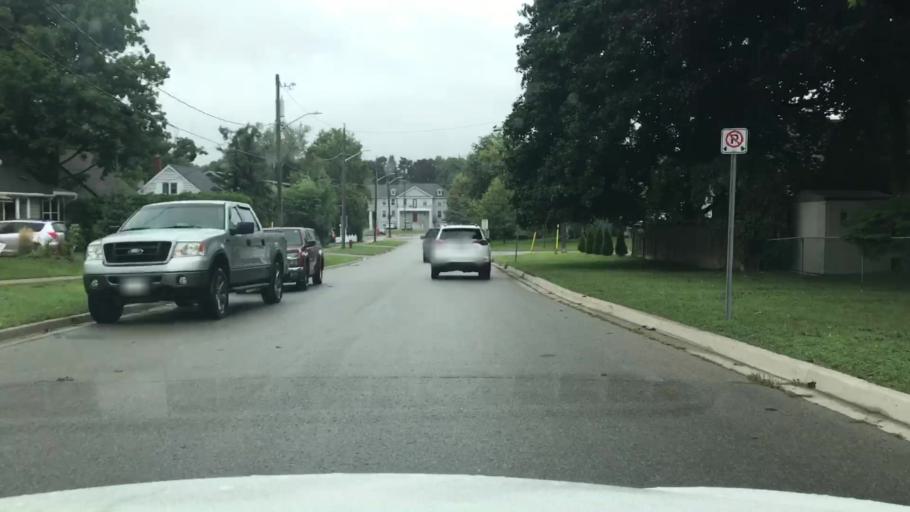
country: CA
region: Ontario
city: Newmarket
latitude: 44.0463
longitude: -79.4670
